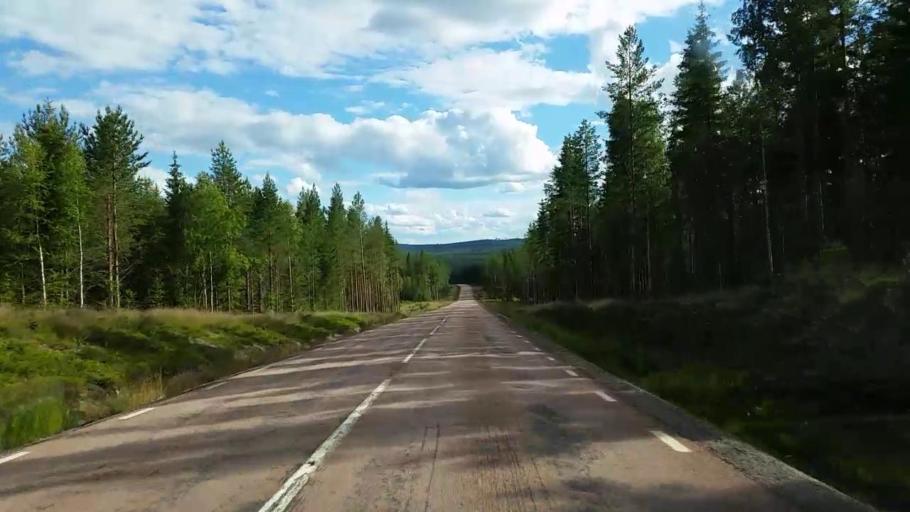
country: SE
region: Gaevleborg
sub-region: Ljusdals Kommun
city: Farila
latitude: 61.9453
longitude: 15.8835
